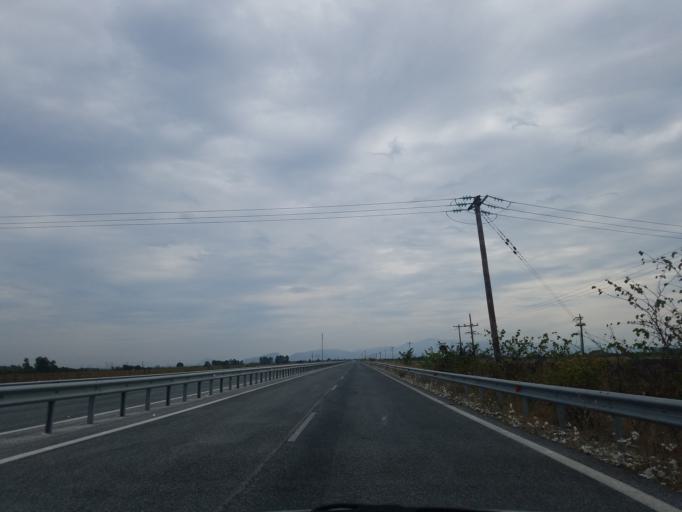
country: GR
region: Thessaly
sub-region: Nomos Kardhitsas
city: Sofades
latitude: 39.2970
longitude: 22.1526
